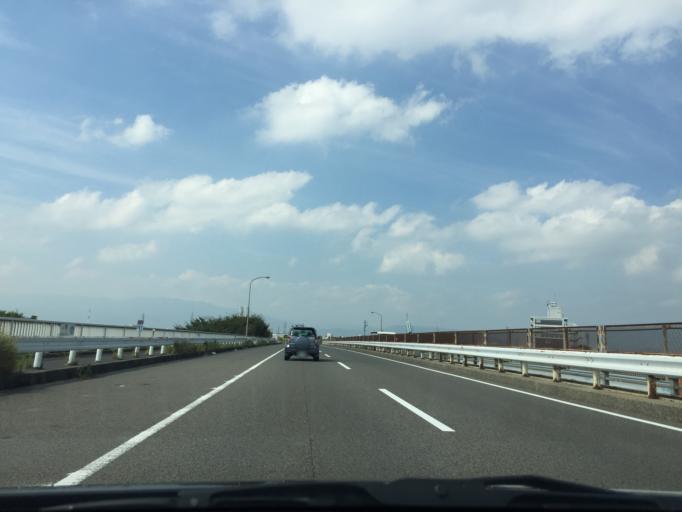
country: JP
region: Gifu
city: Ogaki
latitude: 35.3752
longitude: 136.6563
